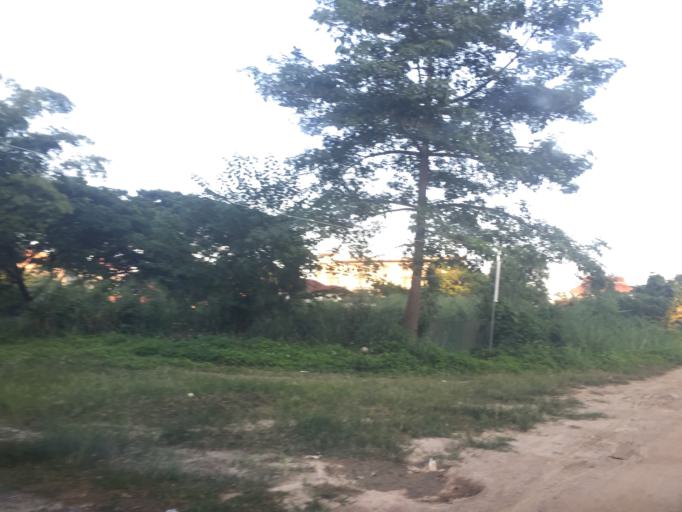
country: TH
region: Chiang Mai
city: Chiang Mai
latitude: 18.8022
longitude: 98.9720
